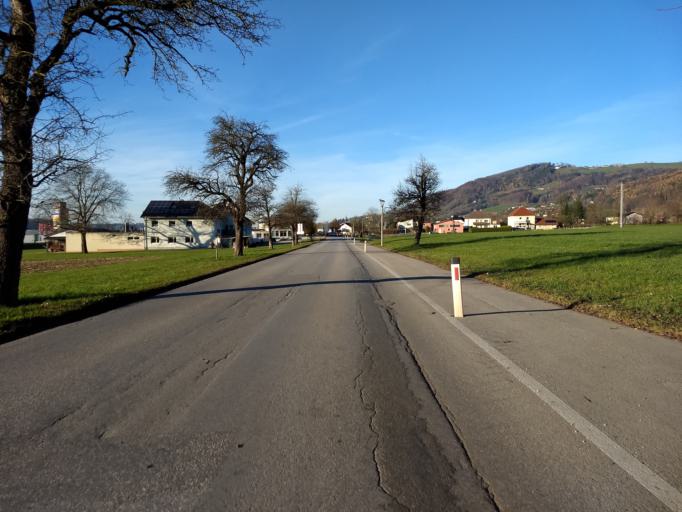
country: AT
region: Upper Austria
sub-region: Politischer Bezirk Kirchdorf an der Krems
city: Micheldorf in Oberoesterreich
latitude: 47.8894
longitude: 14.1308
